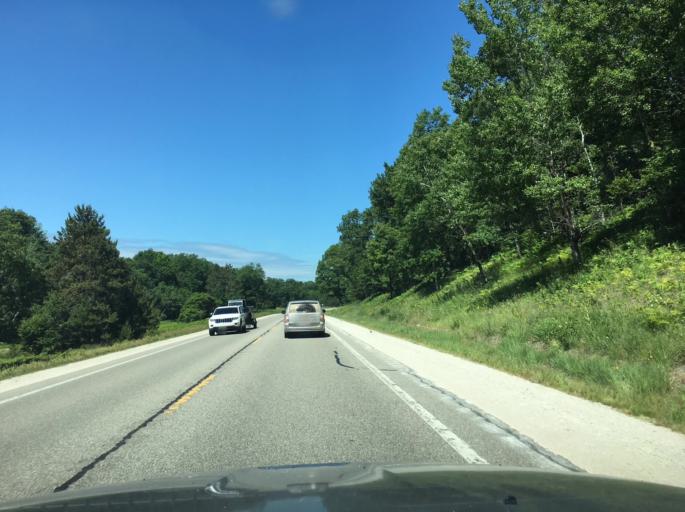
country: US
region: Michigan
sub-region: Osceola County
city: Reed City
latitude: 43.8930
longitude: -85.6765
